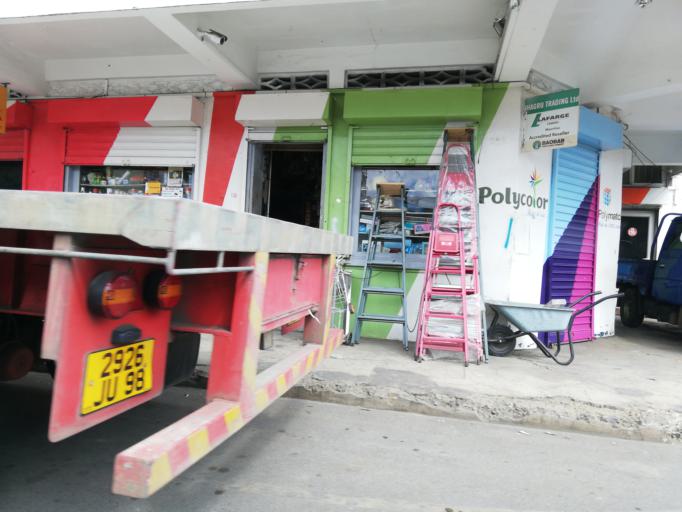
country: MU
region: Black River
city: Petite Riviere
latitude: -20.2173
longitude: 57.4649
